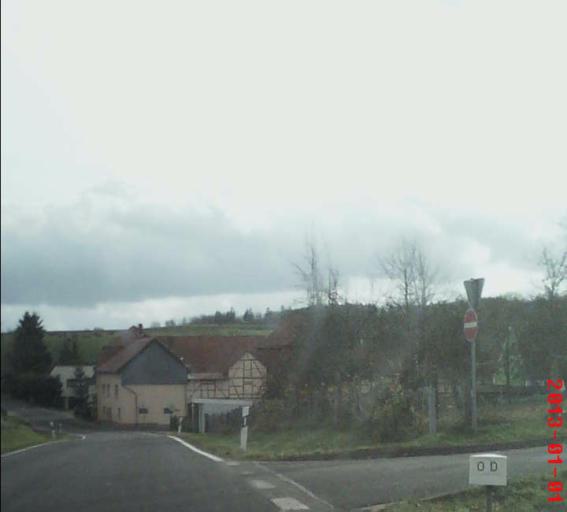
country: DE
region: Thuringia
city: Anrode
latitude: 51.2412
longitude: 10.3725
